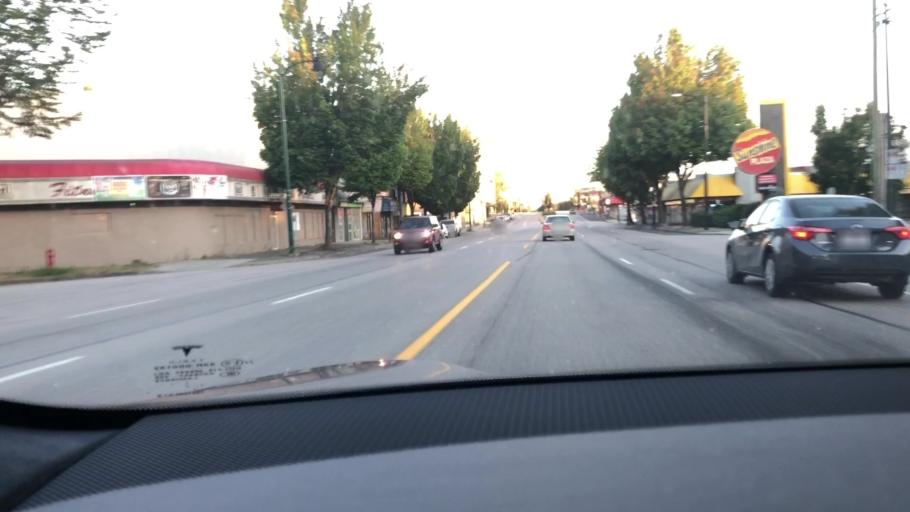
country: CA
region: British Columbia
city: Vancouver
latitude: 49.2473
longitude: -123.0697
